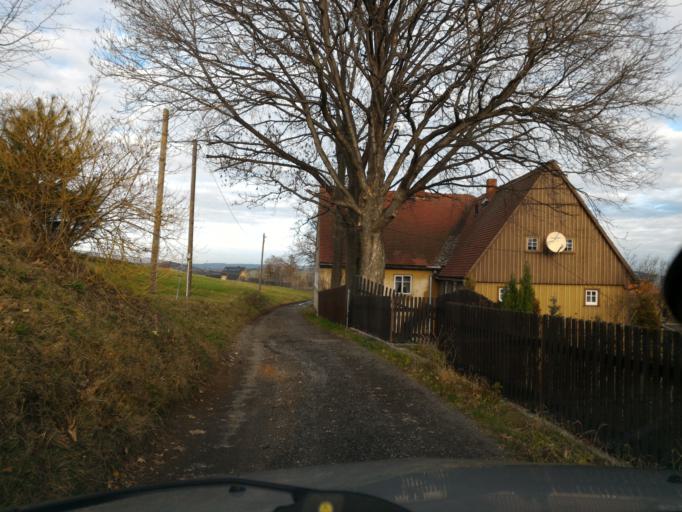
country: DE
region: Saxony
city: Grossschonau
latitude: 50.8686
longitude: 14.6481
